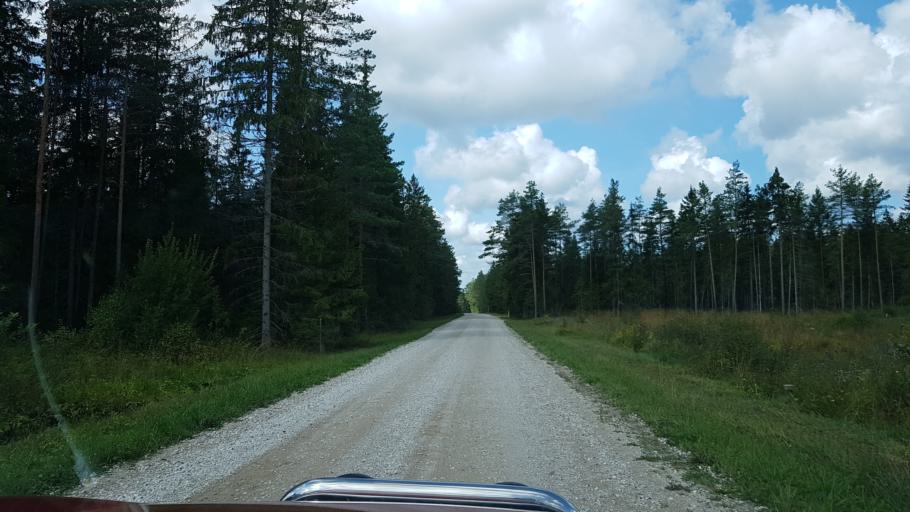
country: EE
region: Raplamaa
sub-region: Rapla vald
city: Rapla
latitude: 58.9554
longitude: 24.6605
